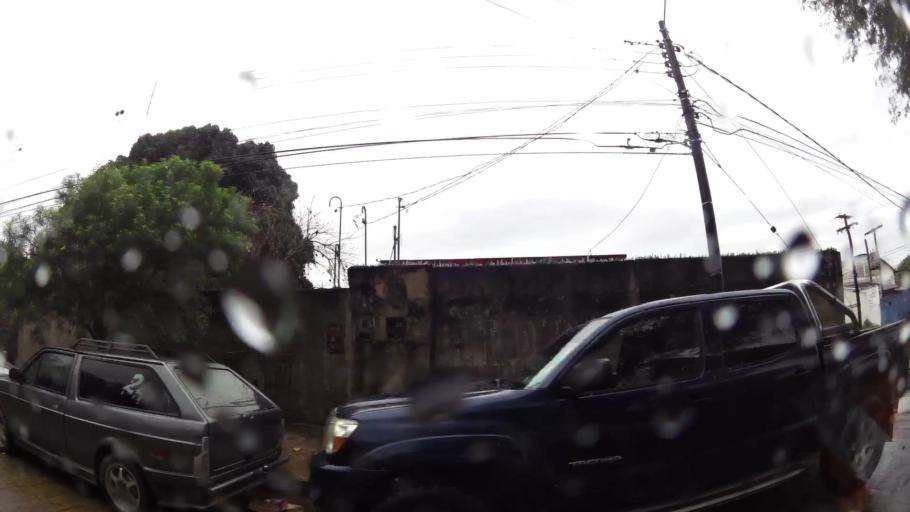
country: BO
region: Santa Cruz
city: Santa Cruz de la Sierra
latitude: -17.8092
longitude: -63.1676
